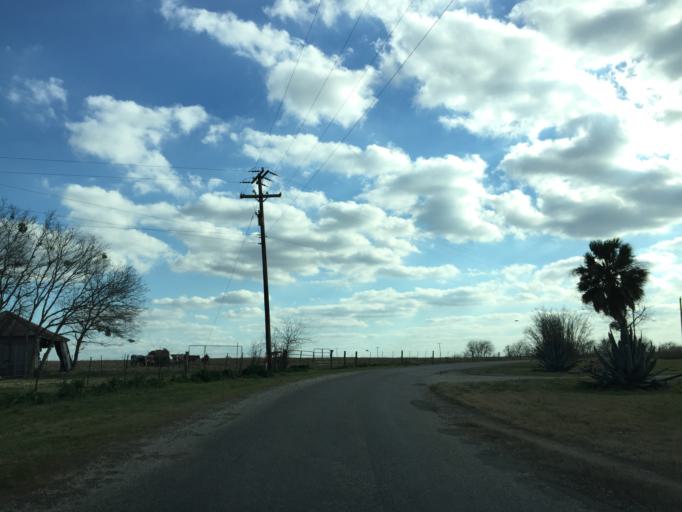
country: US
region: Texas
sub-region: Williamson County
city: Taylor
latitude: 30.6316
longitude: -97.4352
